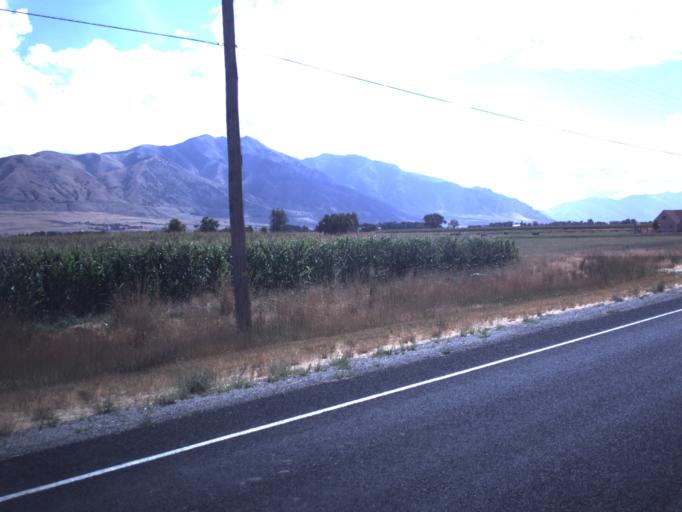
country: US
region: Utah
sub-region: Box Elder County
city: Garland
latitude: 41.7663
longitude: -112.1488
